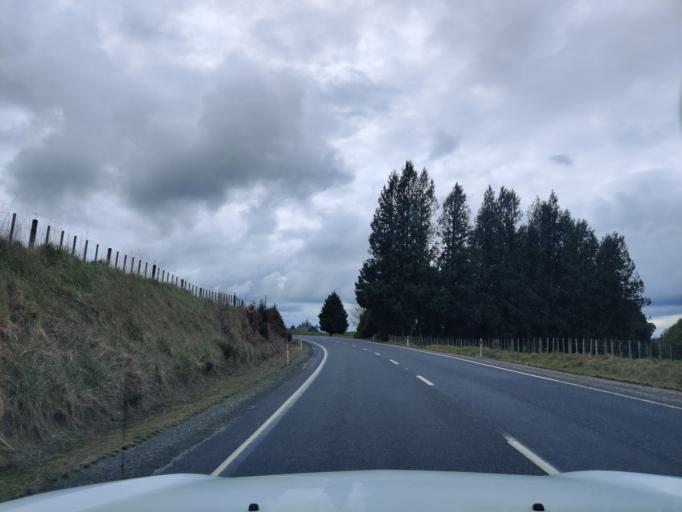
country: NZ
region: Waikato
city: Turangi
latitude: -39.0276
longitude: 175.3825
